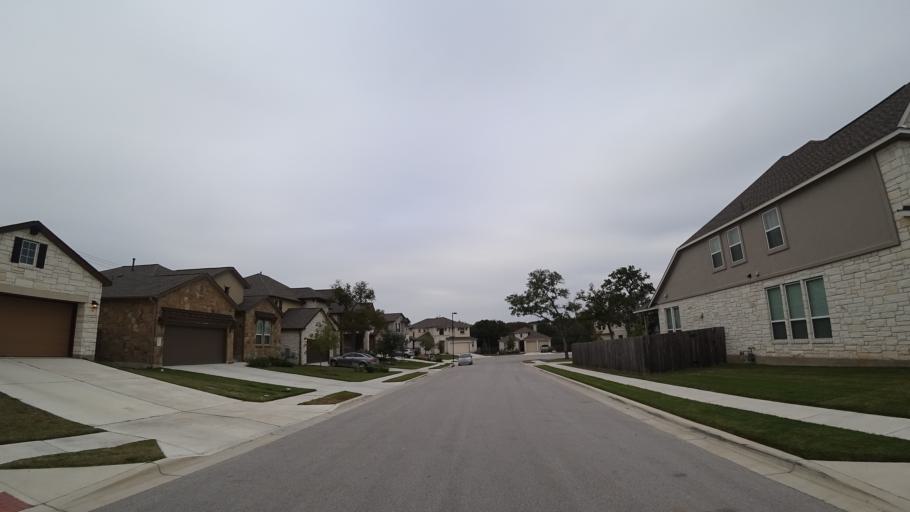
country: US
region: Texas
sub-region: Travis County
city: Shady Hollow
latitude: 30.1841
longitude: -97.8998
